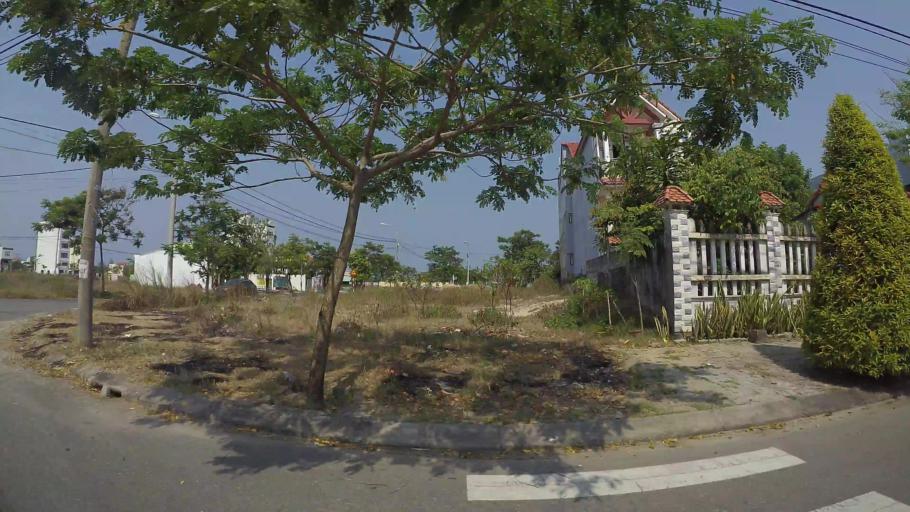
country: VN
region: Da Nang
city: Ngu Hanh Son
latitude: 15.9848
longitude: 108.2710
